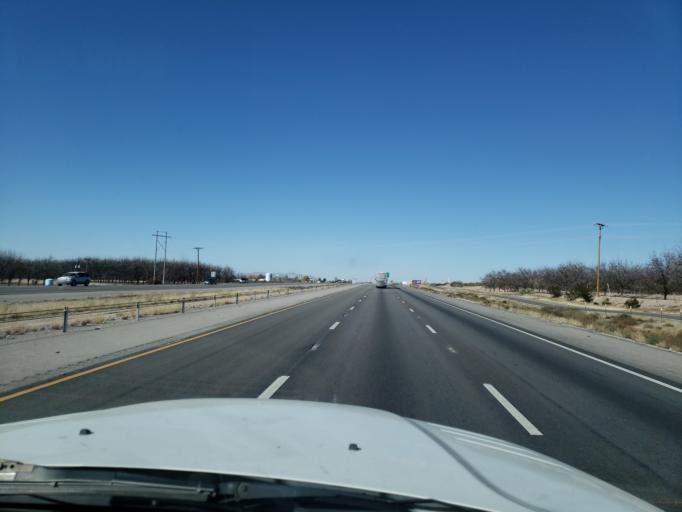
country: US
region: New Mexico
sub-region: Dona Ana County
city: University Park
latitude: 32.2415
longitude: -106.7182
